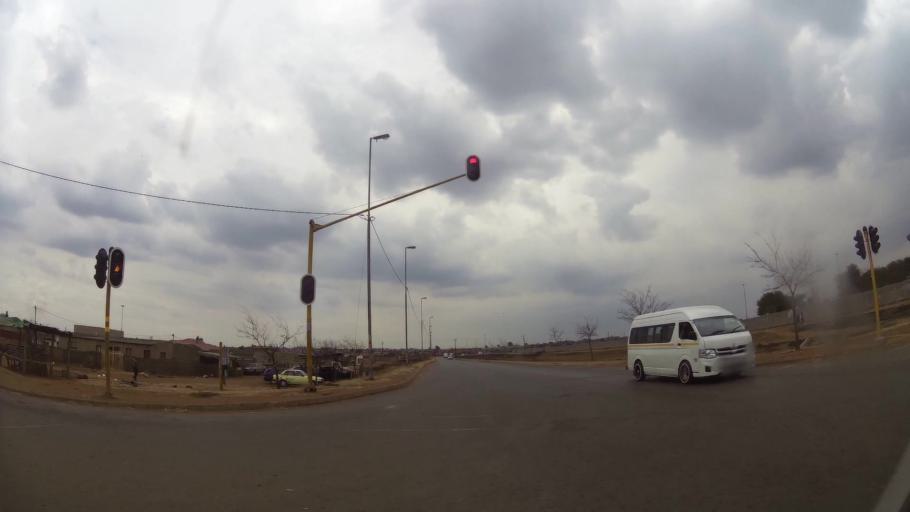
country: ZA
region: Gauteng
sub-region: Ekurhuleni Metropolitan Municipality
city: Germiston
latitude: -26.3709
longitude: 28.1493
